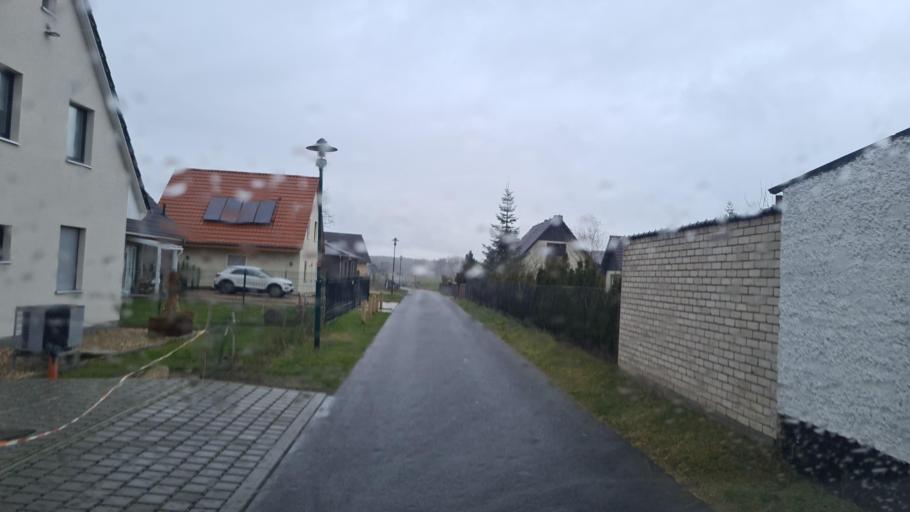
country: DE
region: Brandenburg
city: Oranienburg
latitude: 52.8799
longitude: 13.2302
